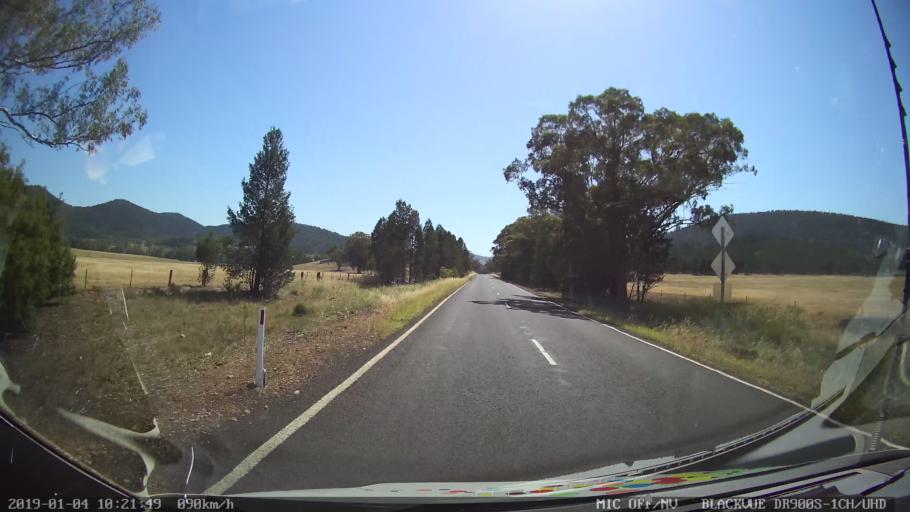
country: AU
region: New South Wales
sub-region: Cabonne
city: Canowindra
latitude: -33.3706
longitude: 148.5155
